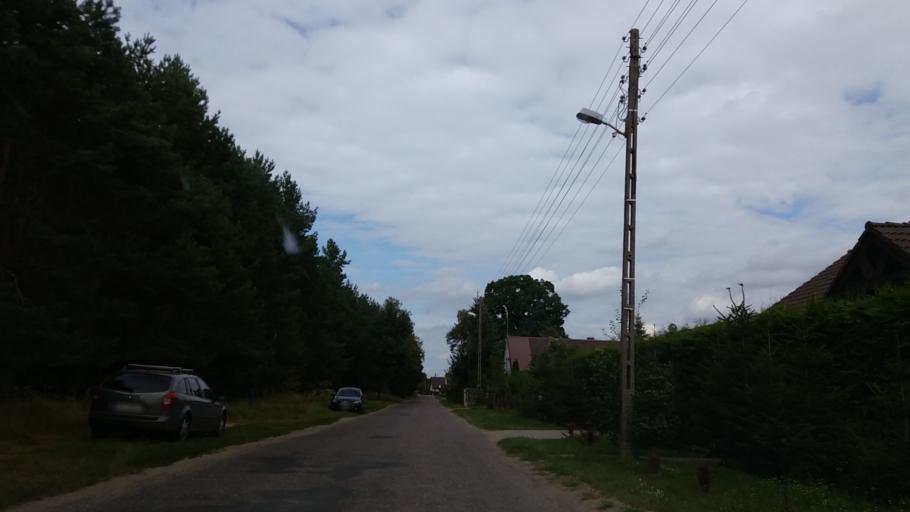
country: PL
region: West Pomeranian Voivodeship
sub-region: Powiat stargardzki
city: Kobylanka
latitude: 53.3390
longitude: 14.8931
